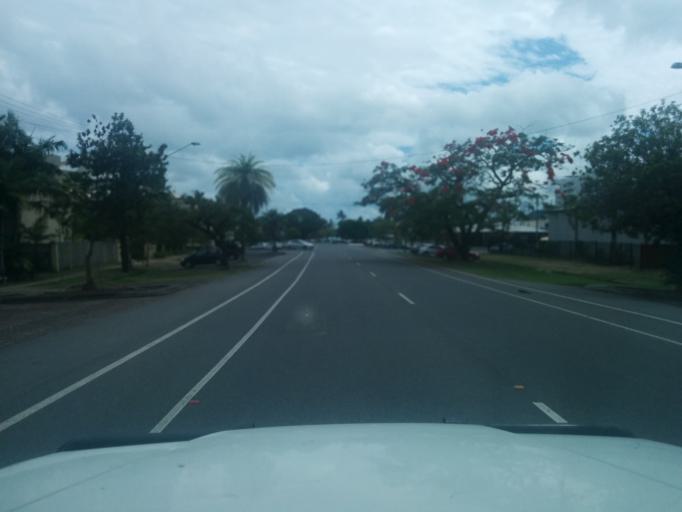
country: AU
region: Queensland
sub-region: Cairns
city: Cairns
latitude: -16.9117
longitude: 145.7644
